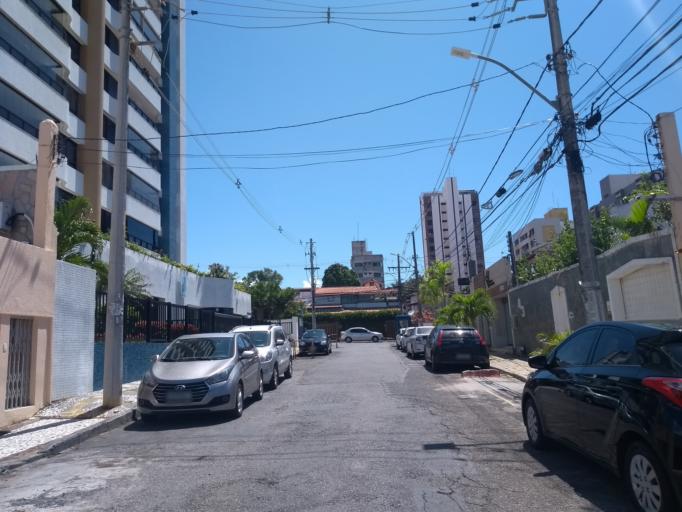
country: BR
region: Bahia
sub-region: Salvador
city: Salvador
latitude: -12.9936
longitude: -38.4586
